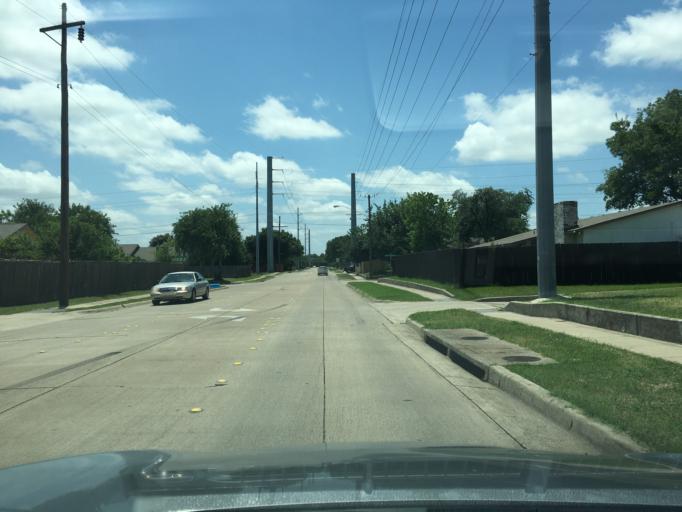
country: US
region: Texas
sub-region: Dallas County
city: Garland
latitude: 32.9557
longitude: -96.6740
